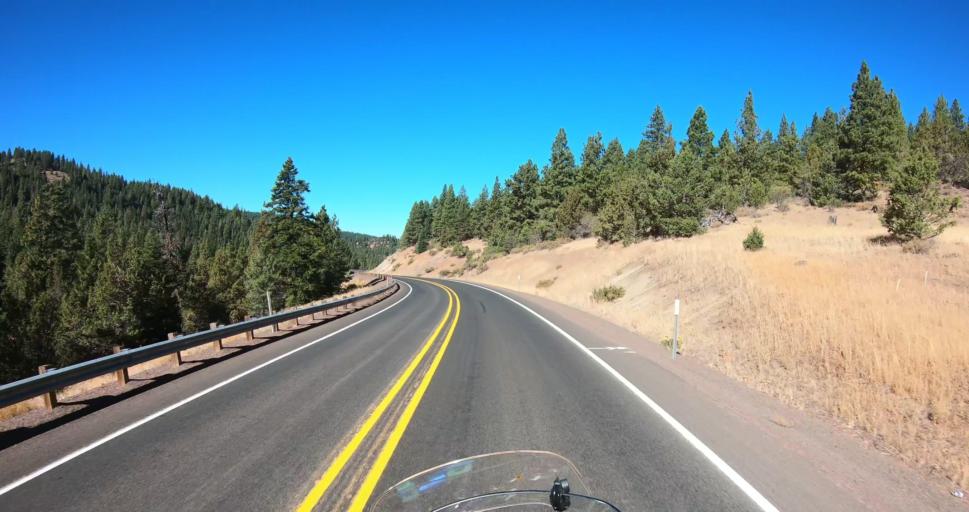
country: US
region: Oregon
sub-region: Lake County
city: Lakeview
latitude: 42.2391
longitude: -120.3025
